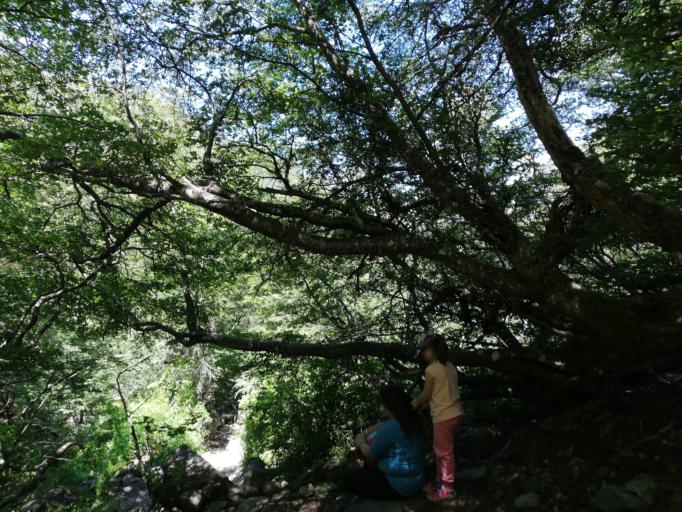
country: AR
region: Neuquen
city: Villa La Angostura
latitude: -41.1908
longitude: -71.8357
